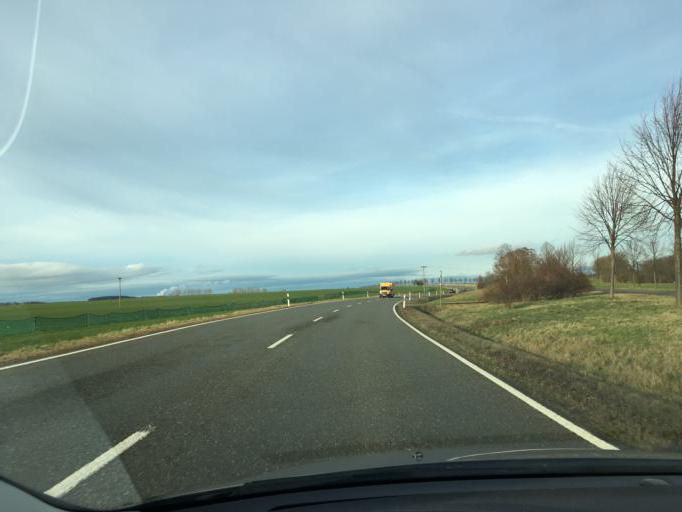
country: DE
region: Thuringia
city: Fockendorf
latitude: 51.0313
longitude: 12.4580
